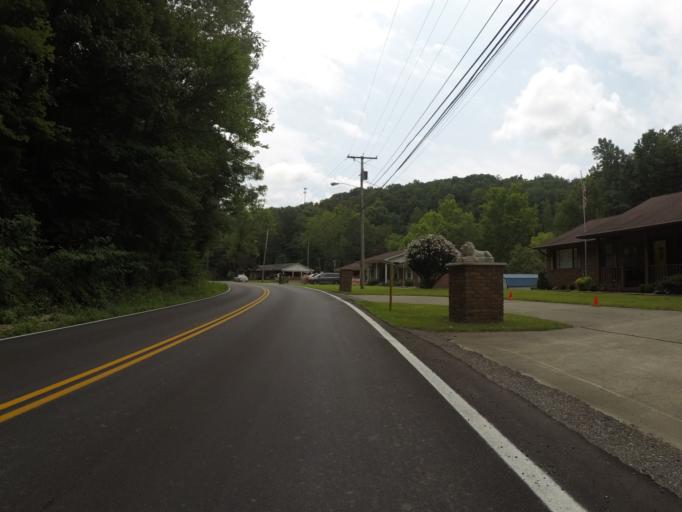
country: US
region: Kentucky
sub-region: Boyd County
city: Ashland
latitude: 38.4374
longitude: -82.6344
